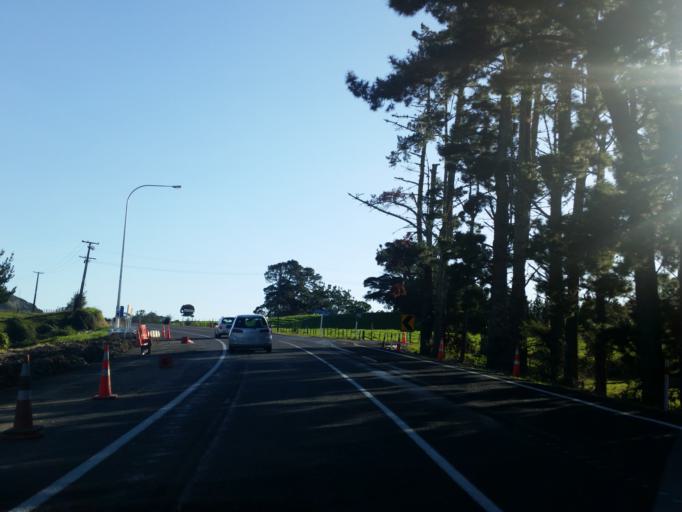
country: NZ
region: Bay of Plenty
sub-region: Western Bay of Plenty District
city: Waihi Beach
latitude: -37.4641
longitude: 175.9370
